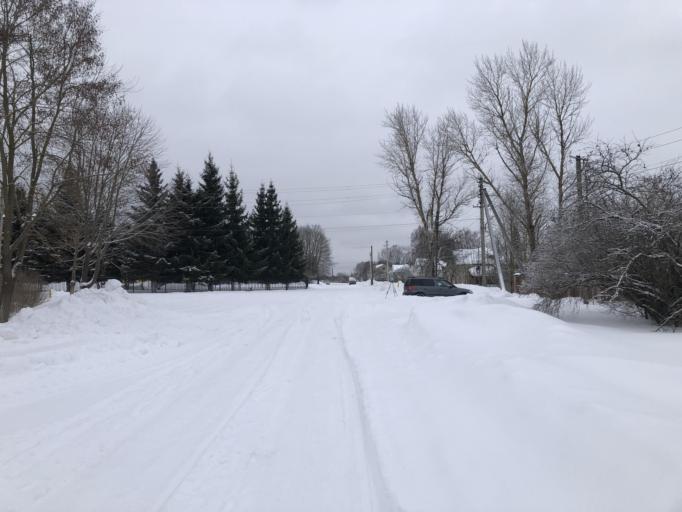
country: RU
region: Smolensk
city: Shatalovo
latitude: 54.3370
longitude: 32.5552
